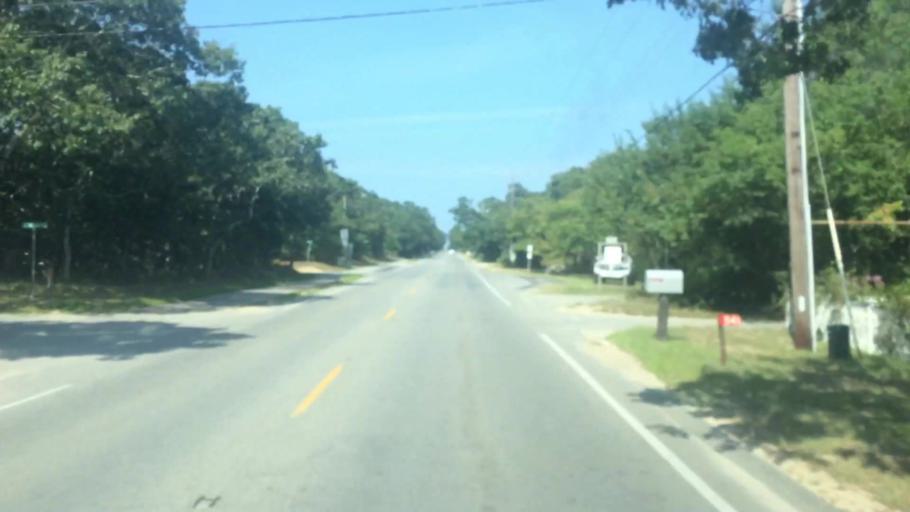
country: US
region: Massachusetts
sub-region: Dukes County
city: Edgartown
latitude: 41.4024
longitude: -70.5542
